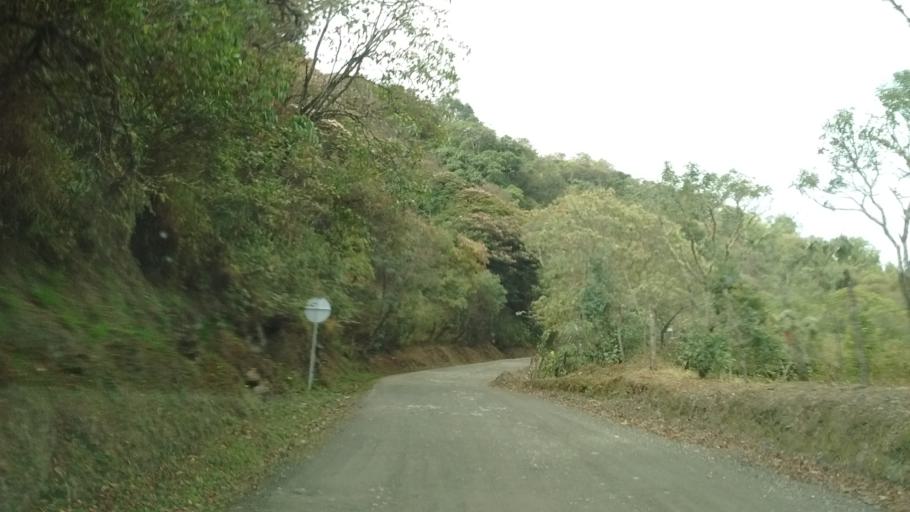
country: CO
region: Cauca
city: Almaguer
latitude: 1.8551
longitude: -76.9464
